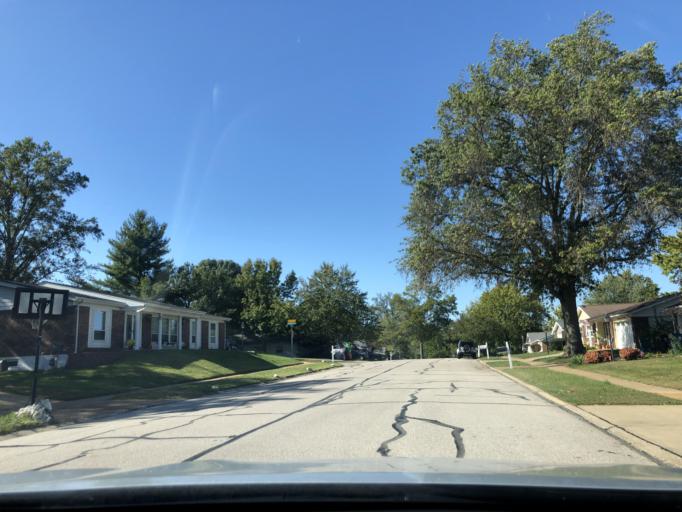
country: US
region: Missouri
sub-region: Saint Louis County
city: Concord
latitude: 38.4964
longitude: -90.3661
